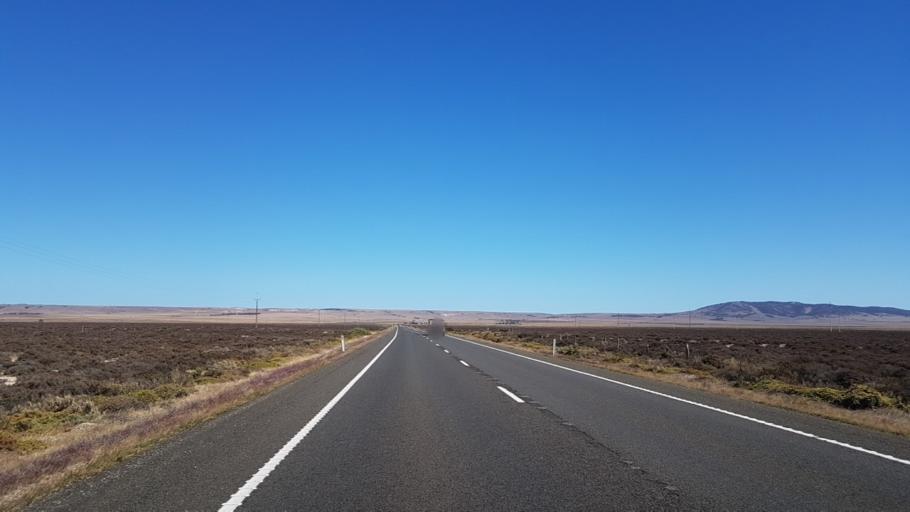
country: AU
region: South Australia
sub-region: Wakefield
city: Balaklava
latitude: -34.1077
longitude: 138.1160
